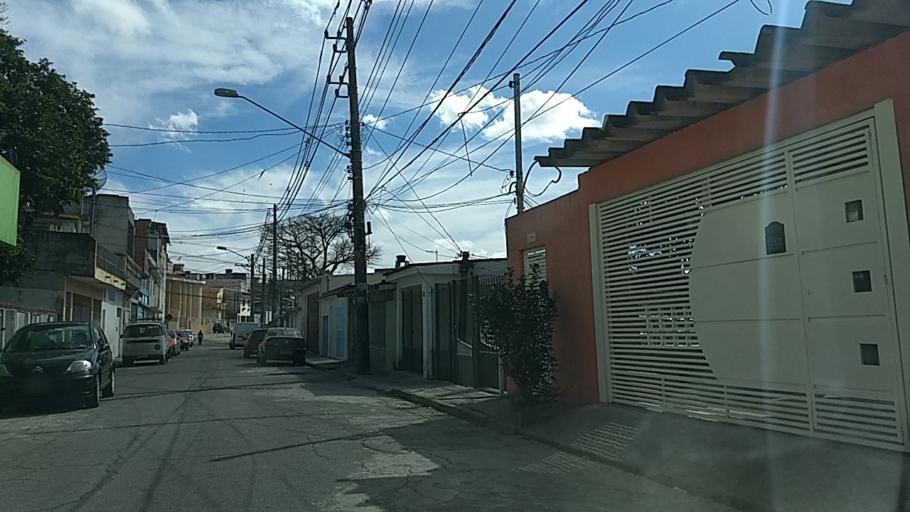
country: BR
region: Sao Paulo
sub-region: Guarulhos
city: Guarulhos
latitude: -23.4890
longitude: -46.5771
